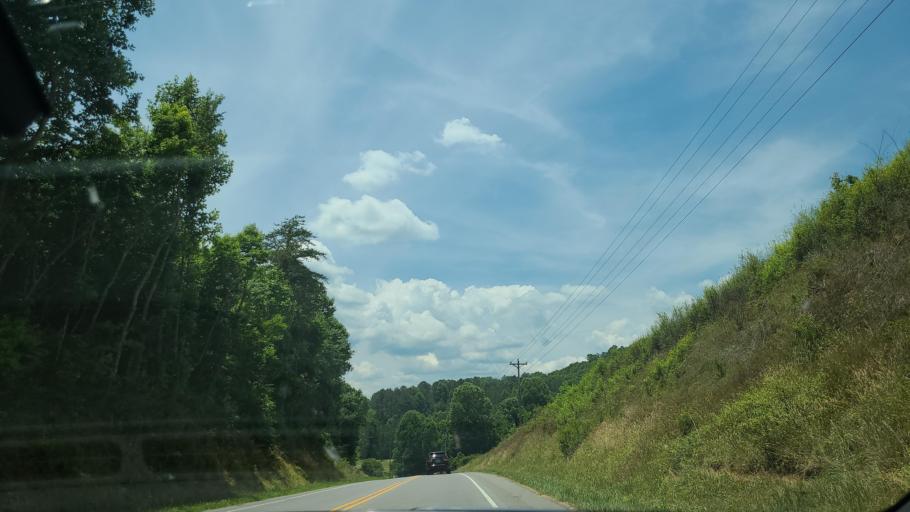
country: US
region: North Carolina
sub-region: Clay County
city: Hayesville
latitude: 35.0530
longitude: -83.9013
